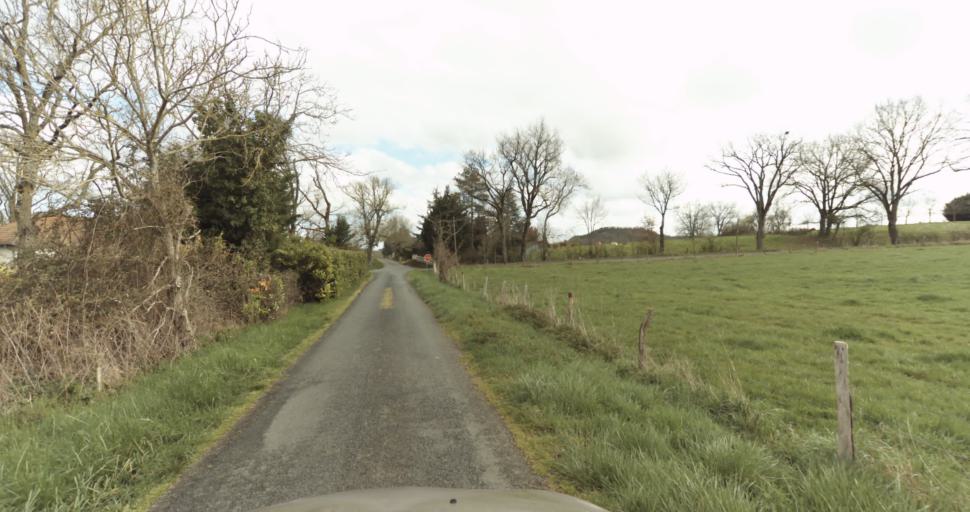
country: FR
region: Midi-Pyrenees
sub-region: Departement du Tarn
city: Frejairolles
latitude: 43.8839
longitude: 2.2006
